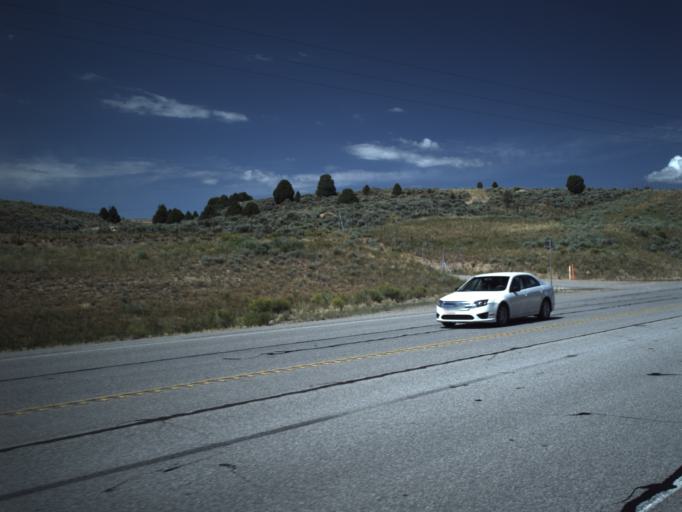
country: US
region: Utah
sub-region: Carbon County
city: Helper
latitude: 39.8297
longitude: -110.9607
